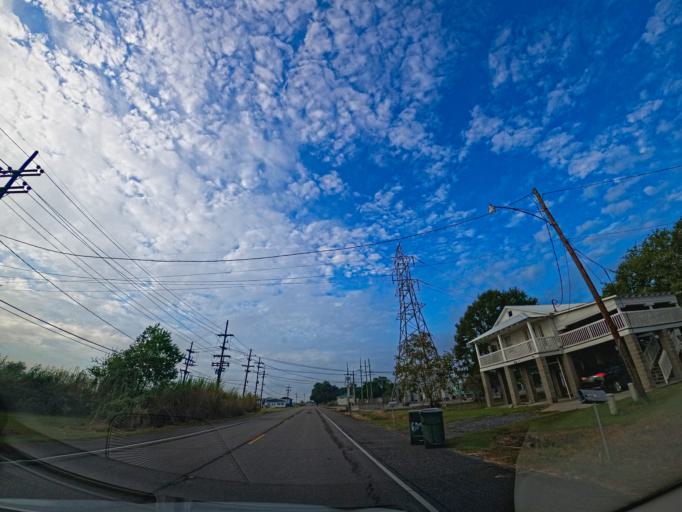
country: US
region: Louisiana
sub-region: Terrebonne Parish
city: Chauvin
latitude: 29.3995
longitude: -90.6105
